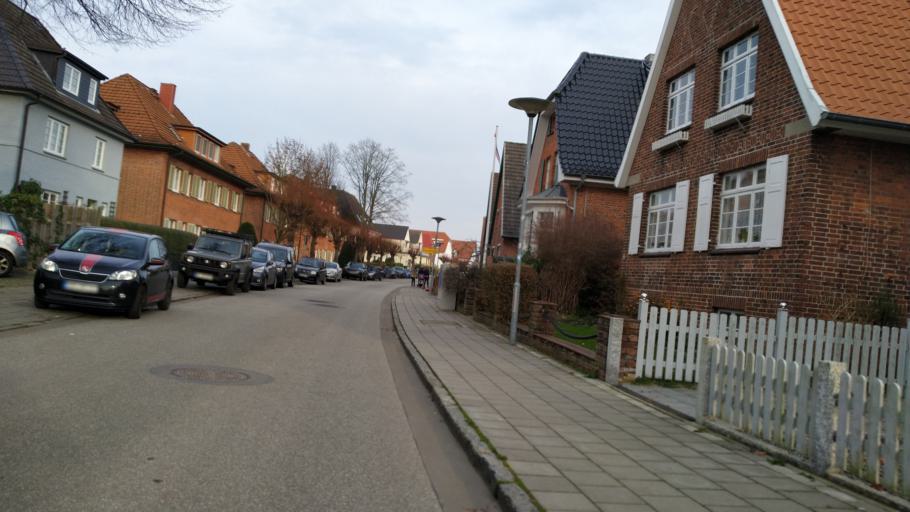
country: DE
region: Schleswig-Holstein
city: Travemuende
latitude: 53.9635
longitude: 10.8724
